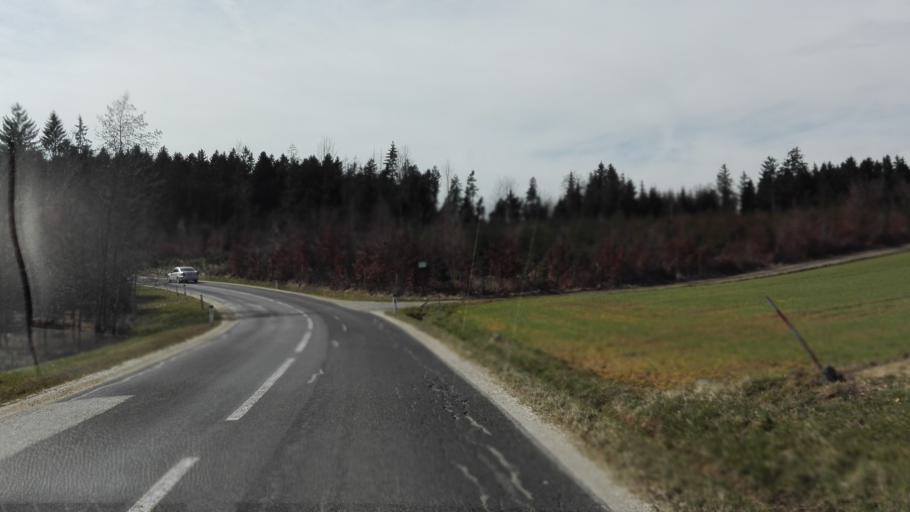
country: AT
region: Upper Austria
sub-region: Politischer Bezirk Scharding
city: Sankt Marienkirchen bei Schaerding
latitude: 48.3749
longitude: 13.6227
